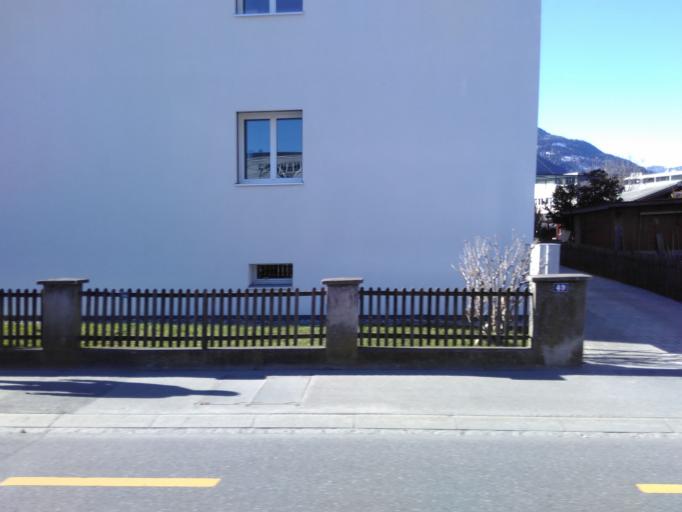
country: CH
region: Grisons
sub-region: Plessur District
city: Chur
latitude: 46.8526
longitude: 9.5144
